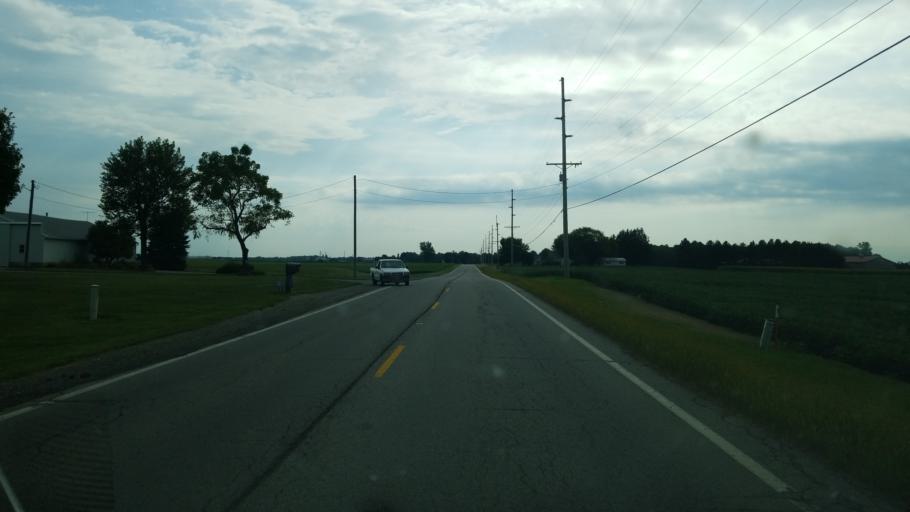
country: US
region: Ohio
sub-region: Richland County
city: Shelby
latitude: 40.8806
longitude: -82.7244
